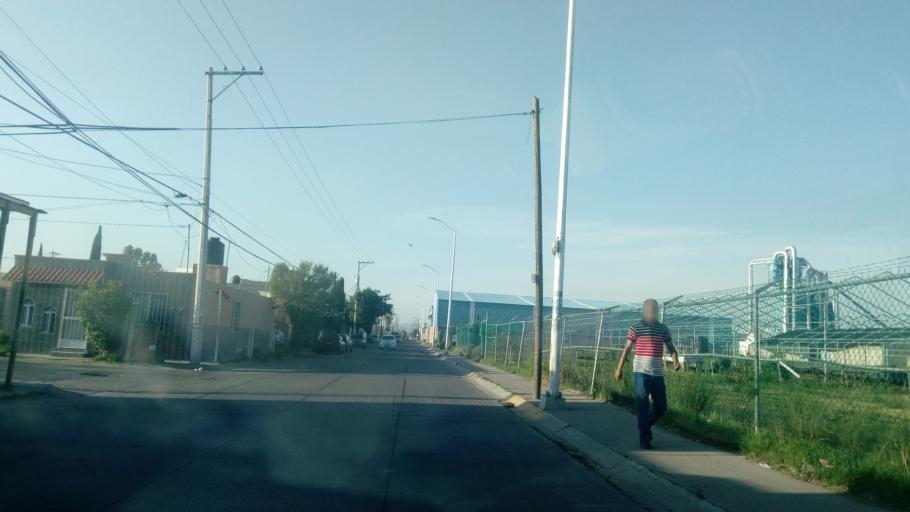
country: MX
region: Durango
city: Victoria de Durango
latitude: 24.0663
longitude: -104.5885
